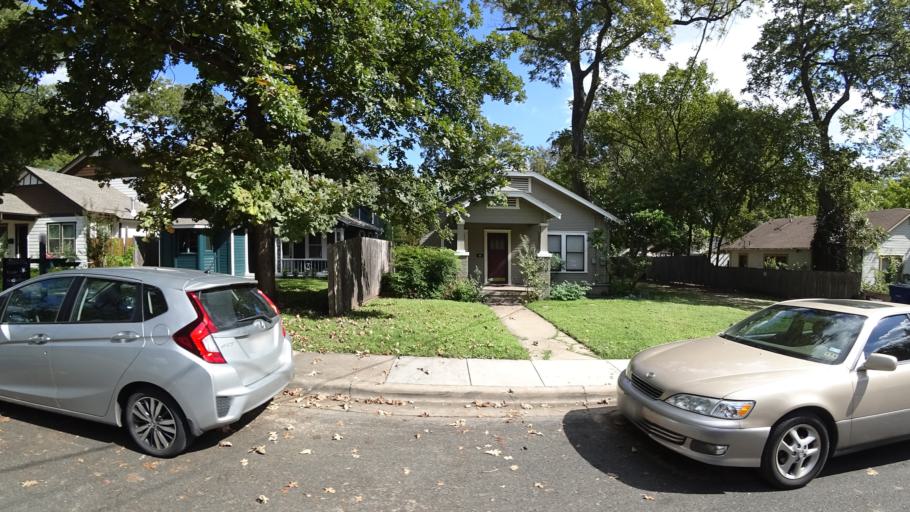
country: US
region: Texas
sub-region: Travis County
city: Austin
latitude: 30.3081
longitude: -97.7251
